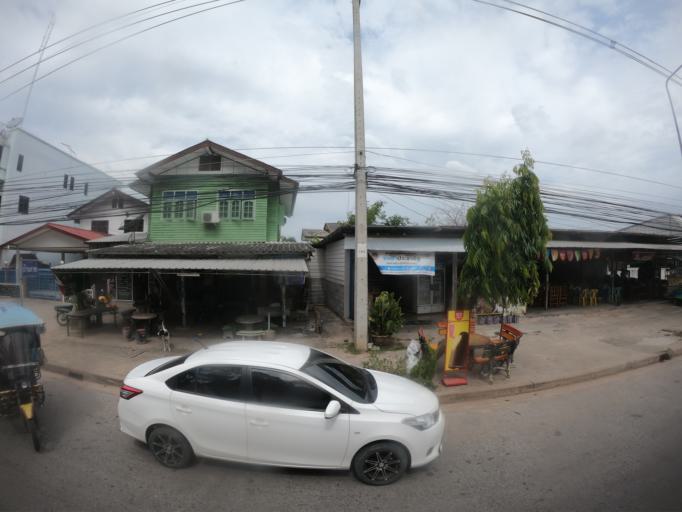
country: TH
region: Roi Et
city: Roi Et
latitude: 16.0604
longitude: 103.6273
